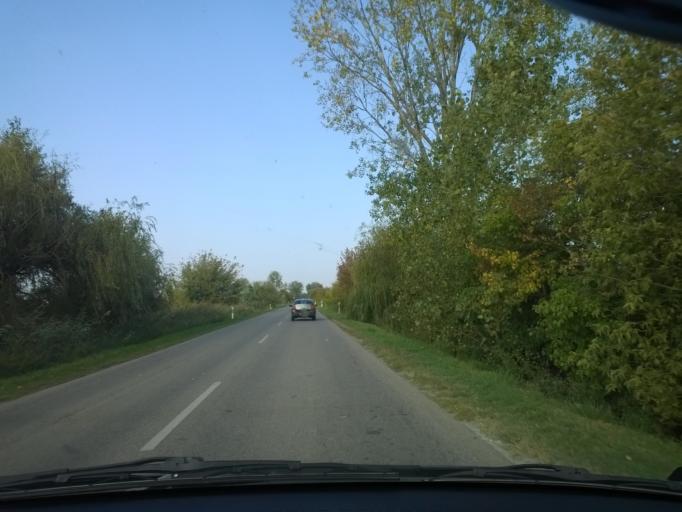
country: HU
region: Bacs-Kiskun
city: Kalocsa
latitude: 46.5092
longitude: 19.0262
